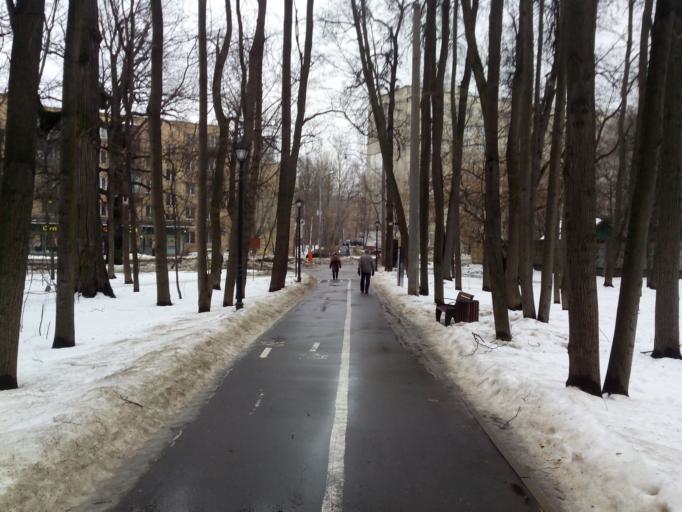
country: RU
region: Moskovskaya
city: Fili
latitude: 55.7422
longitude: 37.4752
